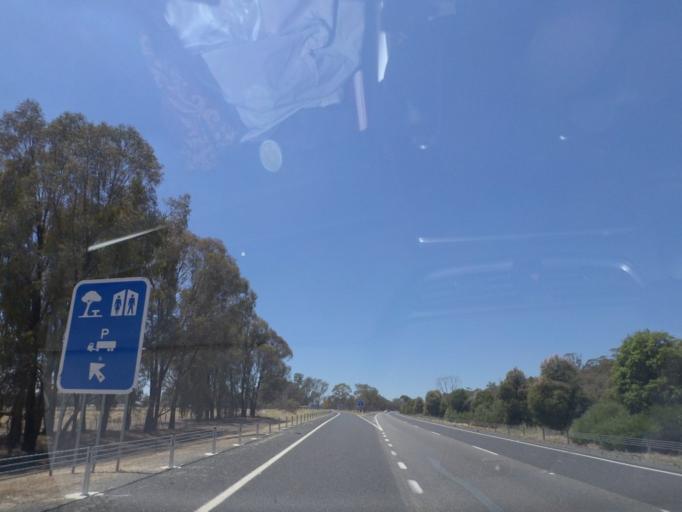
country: AU
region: Victoria
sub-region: Benalla
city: Benalla
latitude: -36.5759
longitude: 145.9265
